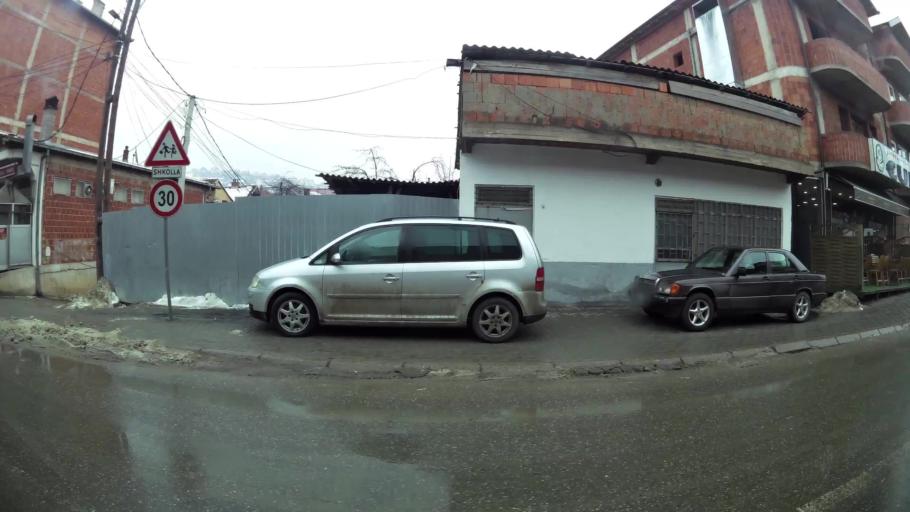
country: XK
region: Pristina
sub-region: Komuna e Prishtines
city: Pristina
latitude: 42.6753
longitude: 21.1688
